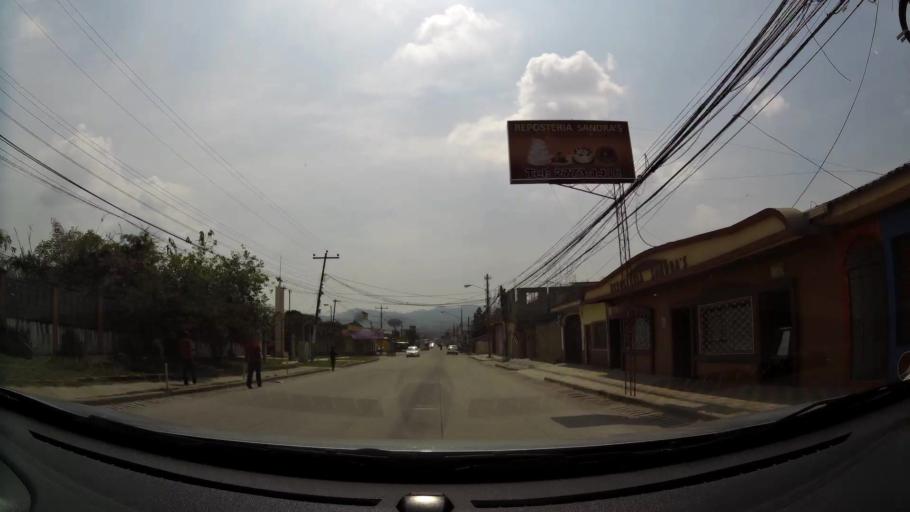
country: HN
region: Comayagua
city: Siguatepeque
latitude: 14.5971
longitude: -87.8387
